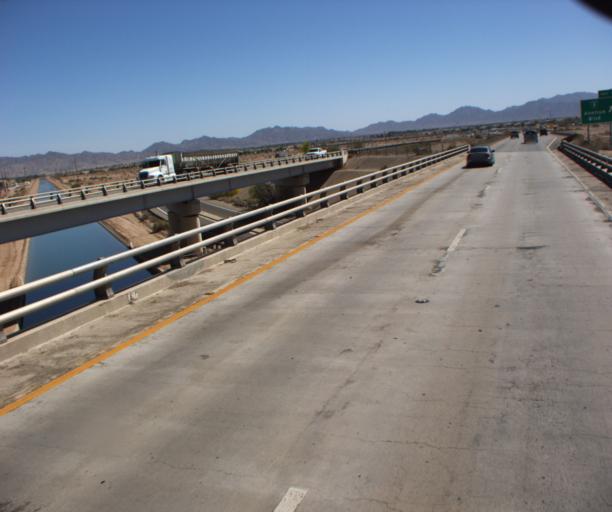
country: US
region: Arizona
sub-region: Yuma County
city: Fortuna Foothills
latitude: 32.6740
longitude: -114.4923
